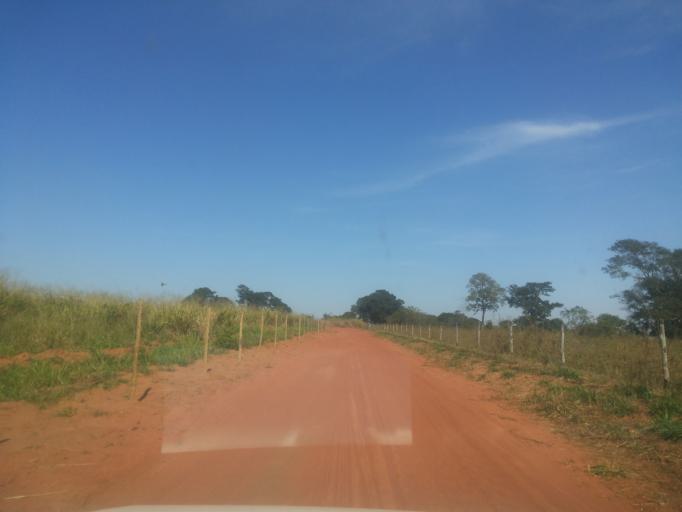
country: BR
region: Minas Gerais
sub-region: Santa Vitoria
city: Santa Vitoria
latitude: -18.9925
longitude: -50.3743
